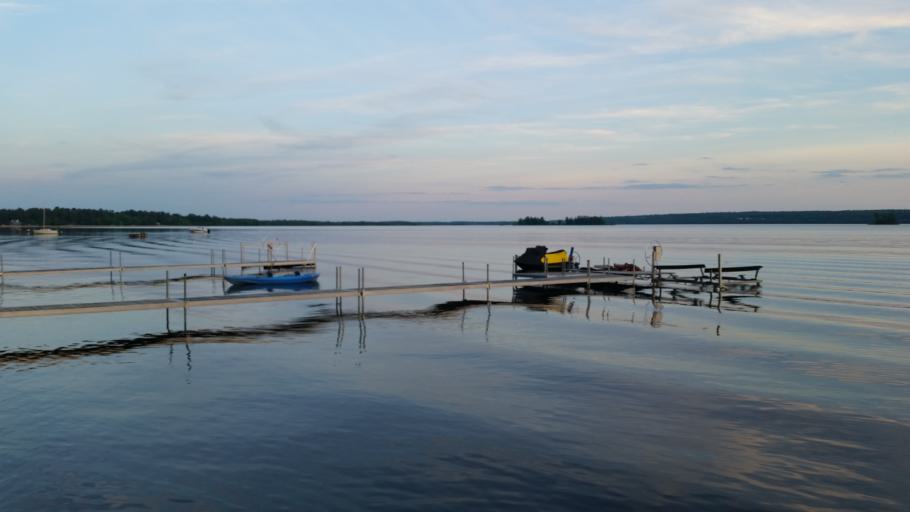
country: CA
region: Quebec
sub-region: Outaouais
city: Shawville
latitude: 45.5175
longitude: -76.4199
